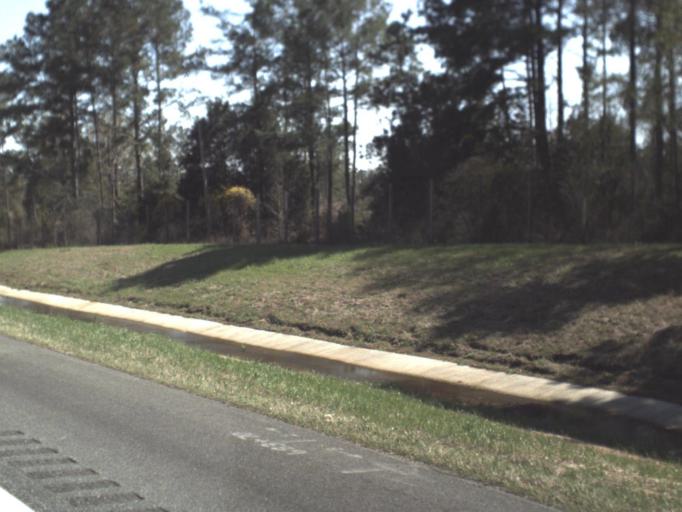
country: US
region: Florida
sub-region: Jackson County
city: Marianna
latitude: 30.7409
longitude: -85.2470
